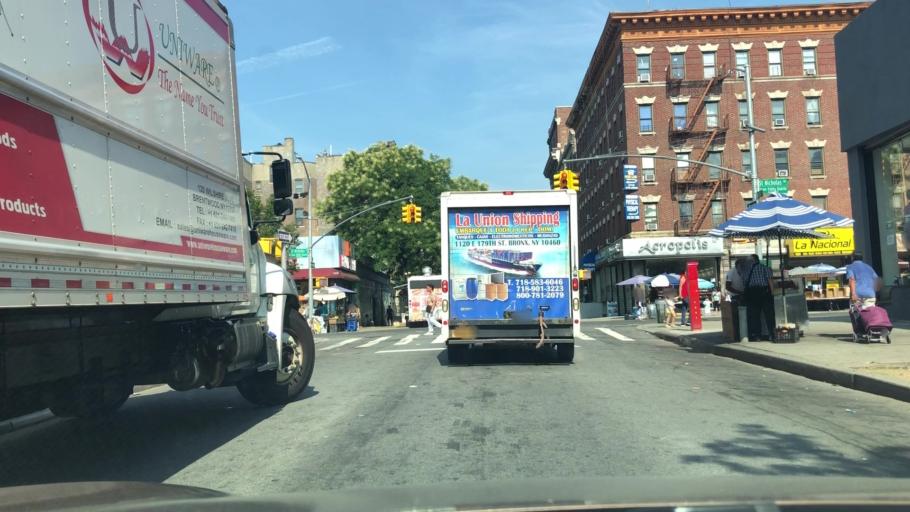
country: US
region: New York
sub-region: New York County
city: Inwood
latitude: 40.8497
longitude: -73.9329
